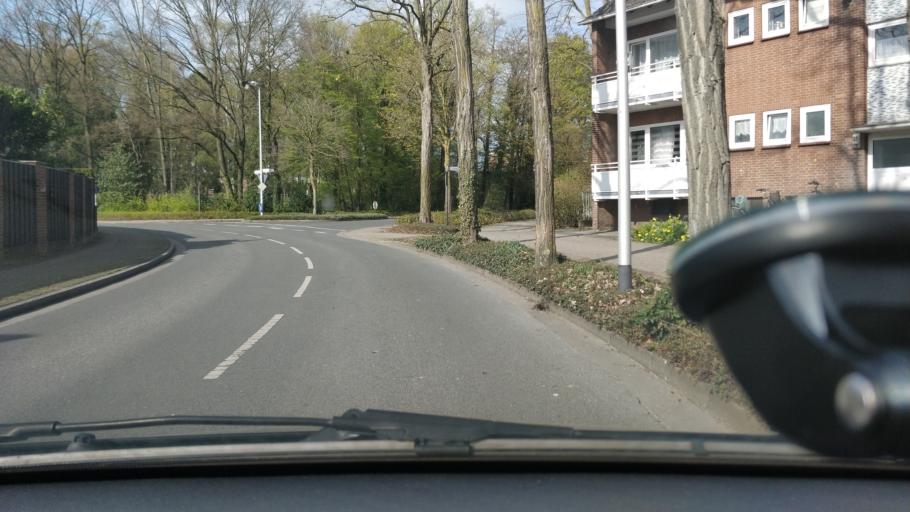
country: DE
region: North Rhine-Westphalia
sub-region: Regierungsbezirk Dusseldorf
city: Bocholt
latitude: 51.8521
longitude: 6.6359
